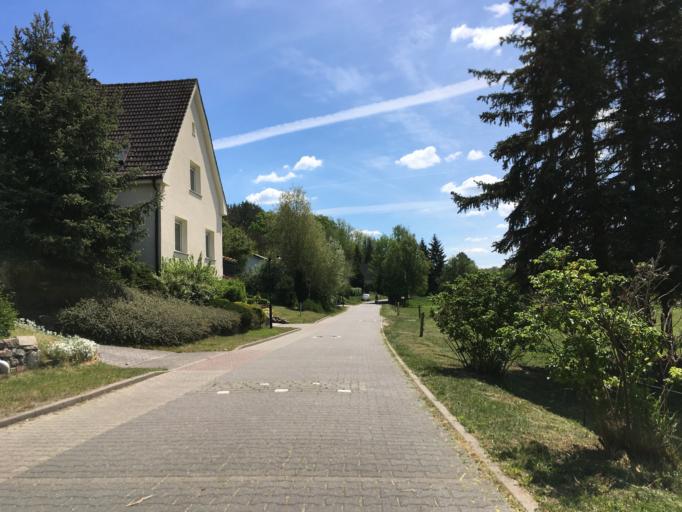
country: DE
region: Brandenburg
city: Niederfinow
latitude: 52.8444
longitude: 13.8969
